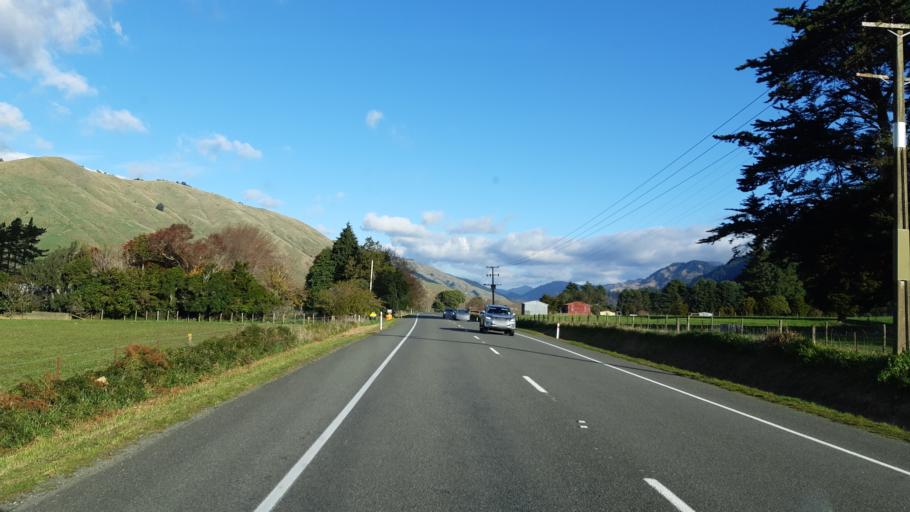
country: NZ
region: Marlborough
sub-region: Marlborough District
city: Picton
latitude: -41.3007
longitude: 173.7704
